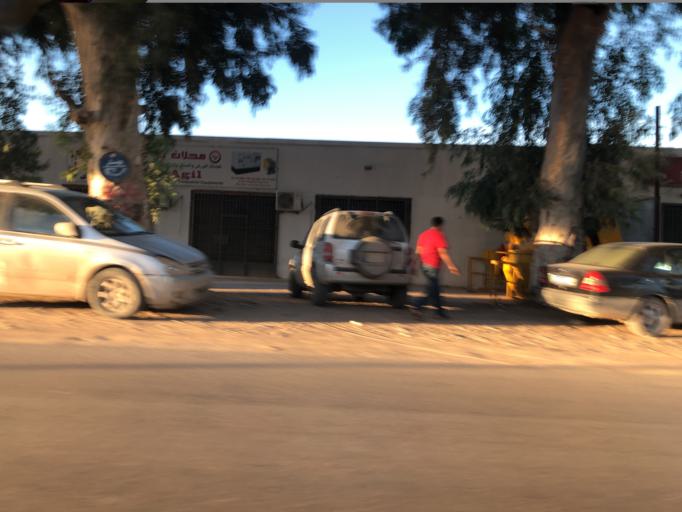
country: LY
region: Tripoli
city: Tagiura
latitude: 32.8700
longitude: 13.2962
